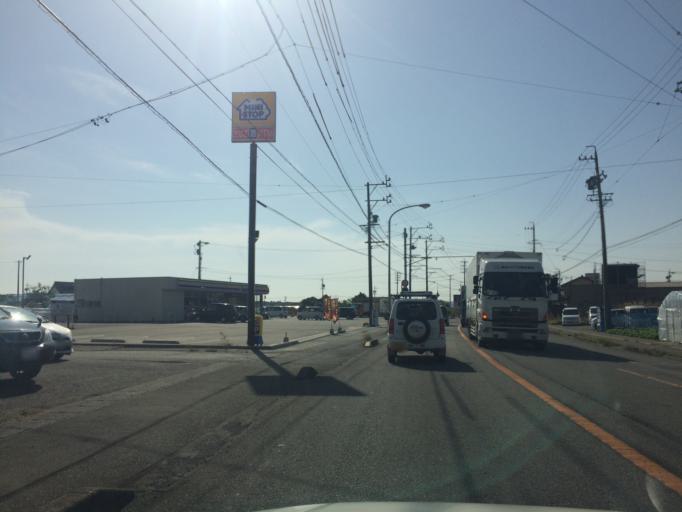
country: JP
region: Shizuoka
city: Sagara
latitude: 34.7428
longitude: 138.2369
